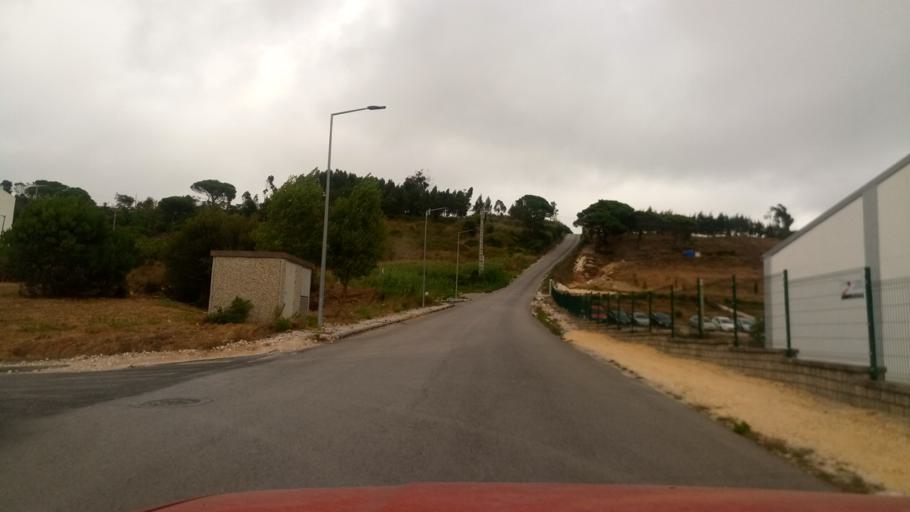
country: PT
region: Leiria
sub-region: Caldas da Rainha
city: Caldas da Rainha
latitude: 39.4217
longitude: -9.1306
